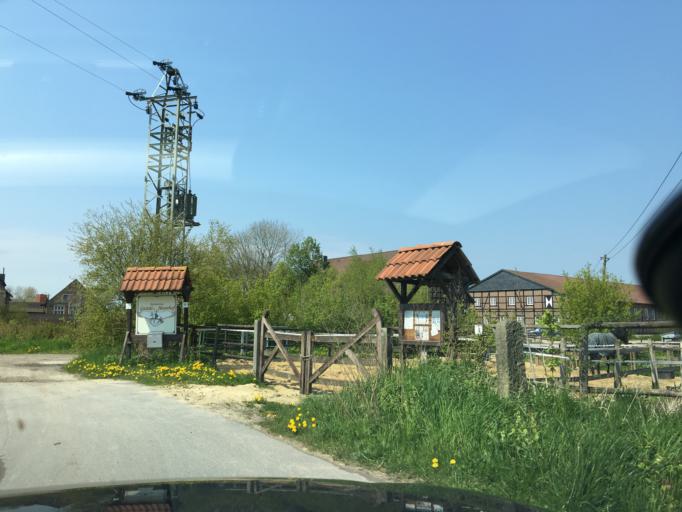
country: DE
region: North Rhine-Westphalia
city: Ludinghausen
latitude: 51.8116
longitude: 7.4540
